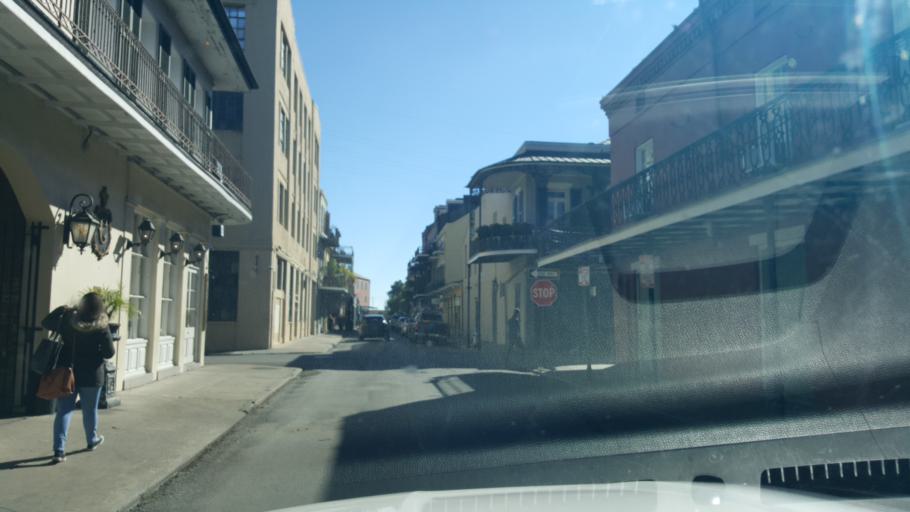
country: US
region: Louisiana
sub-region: Orleans Parish
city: New Orleans
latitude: 29.9600
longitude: -90.0620
